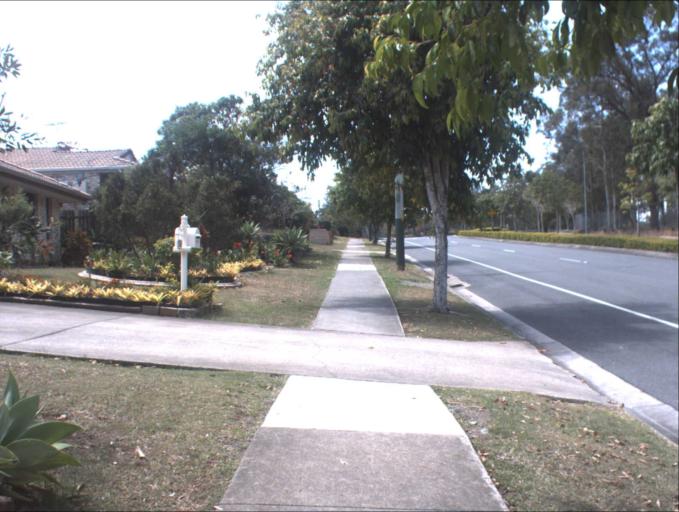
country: AU
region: Queensland
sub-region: Logan
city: Slacks Creek
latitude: -27.6380
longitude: 153.1469
